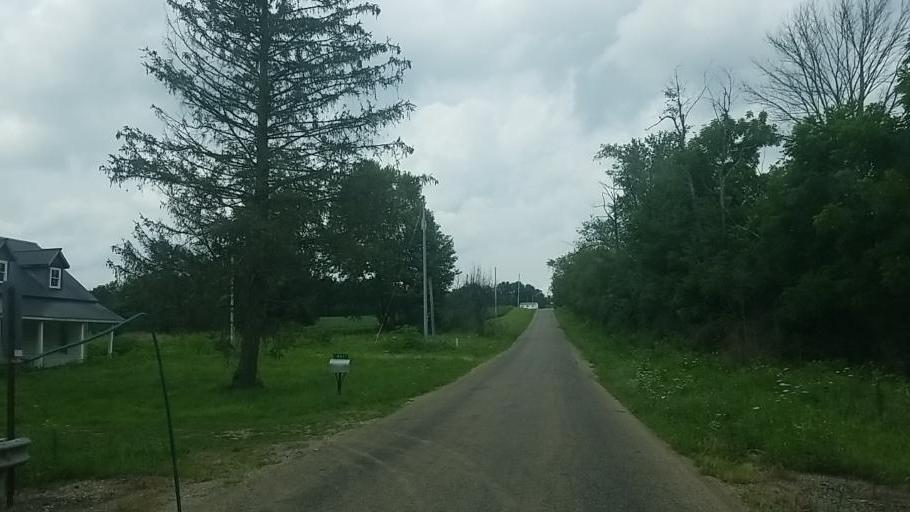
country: US
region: Ohio
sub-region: Licking County
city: Utica
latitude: 40.2425
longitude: -82.3371
